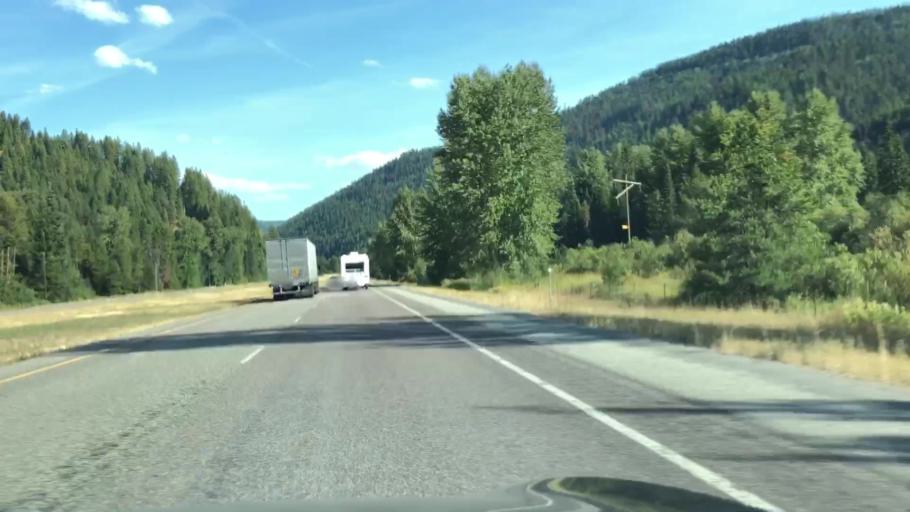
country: US
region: Montana
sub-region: Sanders County
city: Thompson Falls
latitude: 47.3641
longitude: -115.3263
